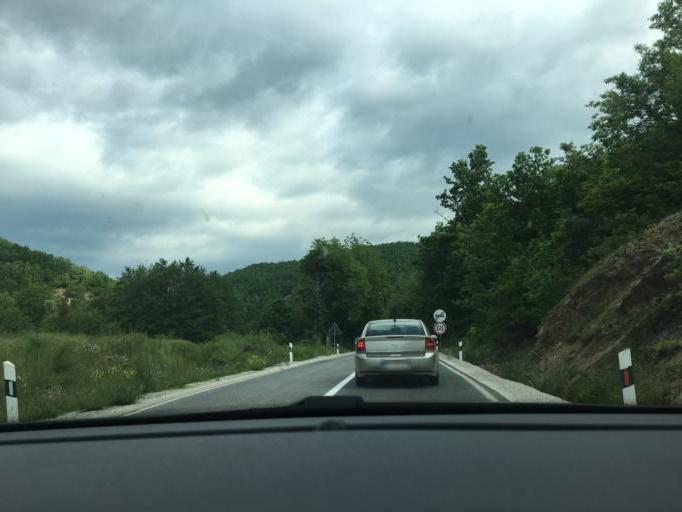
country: MK
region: Resen
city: Jankovec
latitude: 41.1358
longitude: 21.0059
